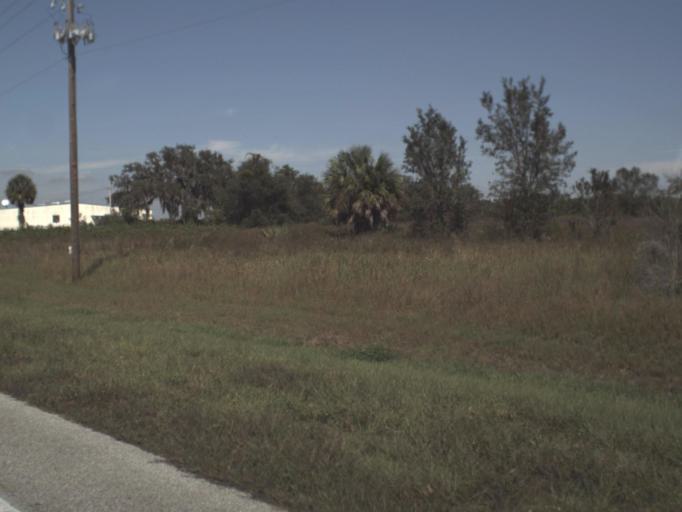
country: US
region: Florida
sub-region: Highlands County
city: Sebring
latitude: 27.4206
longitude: -81.4171
